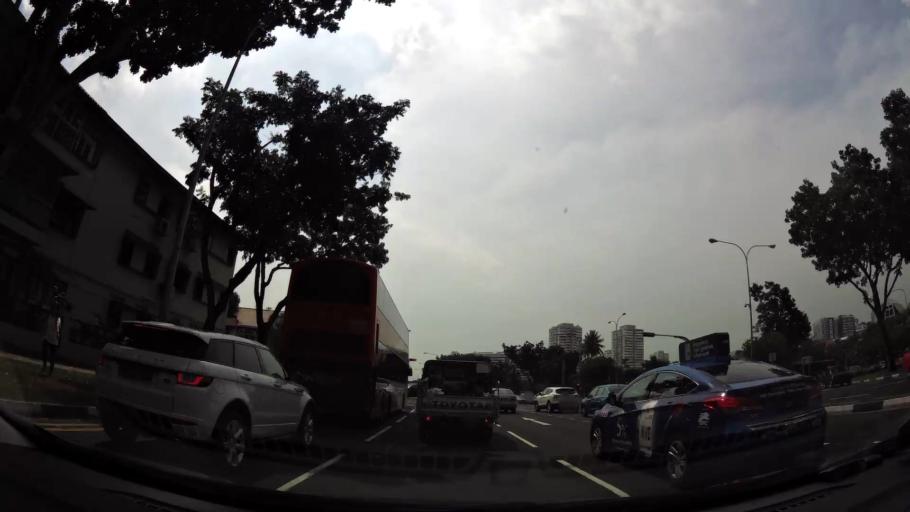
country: SG
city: Singapore
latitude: 1.3086
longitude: 103.9085
